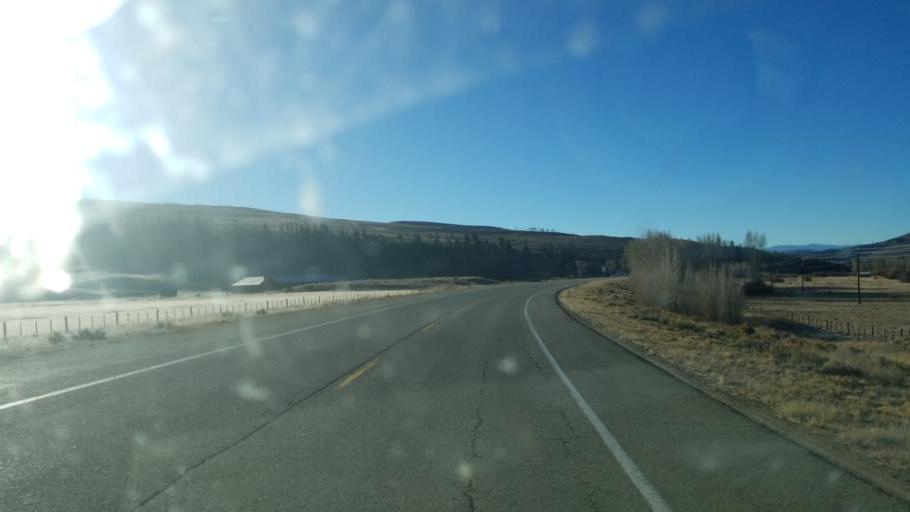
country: US
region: Colorado
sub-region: Gunnison County
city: Gunnison
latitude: 38.7239
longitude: -106.8485
